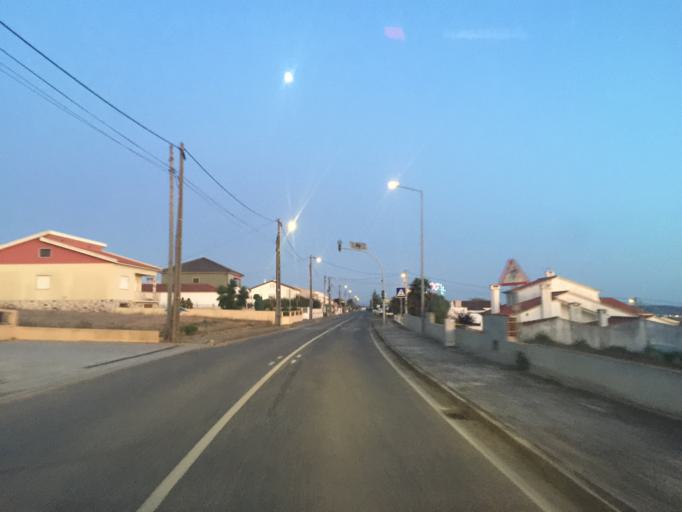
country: PT
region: Lisbon
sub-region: Lourinha
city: Lourinha
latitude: 39.2845
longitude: -9.3030
